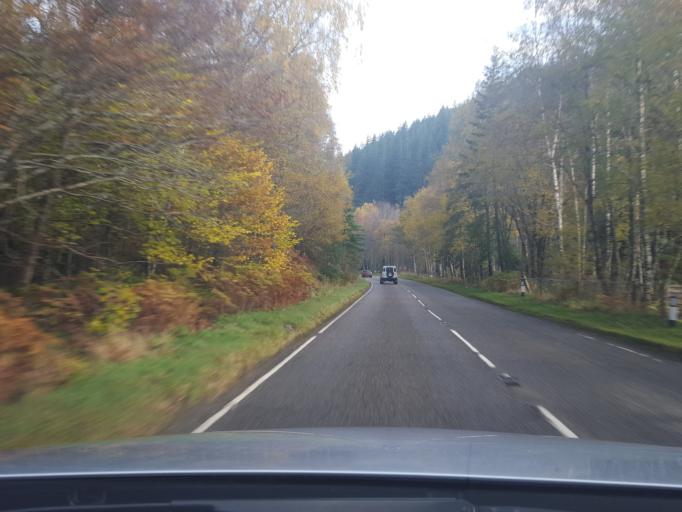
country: GB
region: Scotland
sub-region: Highland
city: Beauly
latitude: 57.2104
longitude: -4.6831
